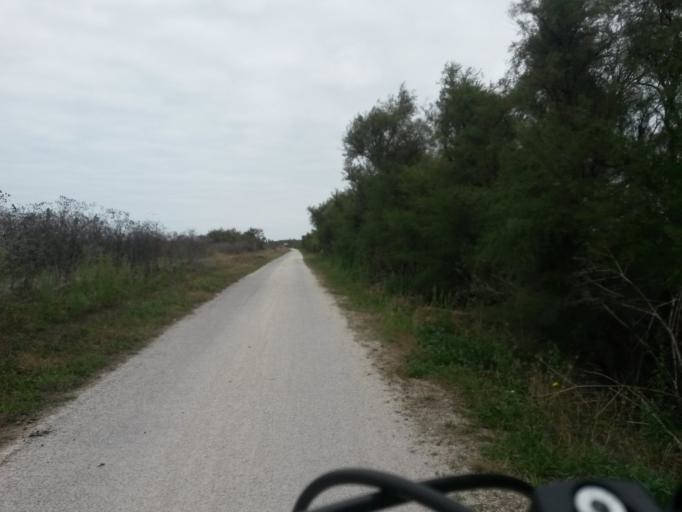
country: FR
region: Poitou-Charentes
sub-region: Departement de la Charente-Maritime
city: Saint-Denis-d'Oleron
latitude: 46.0075
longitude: -1.3846
